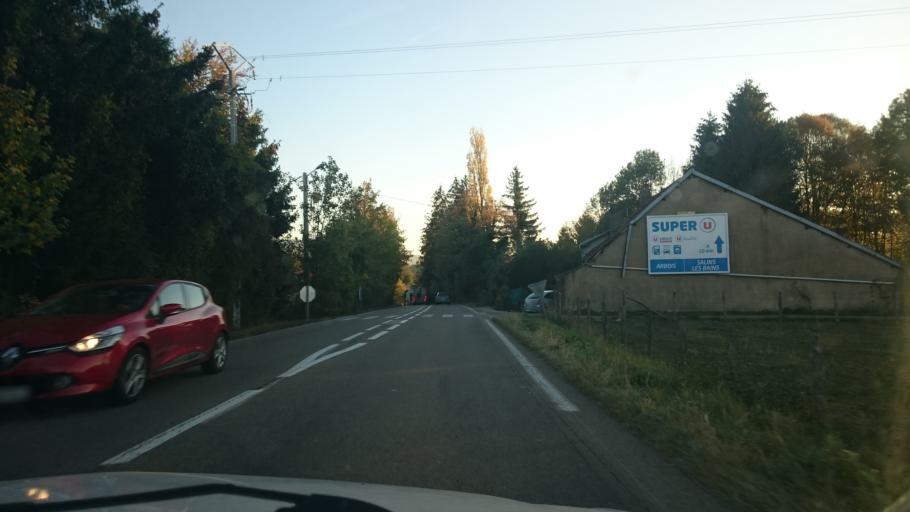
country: FR
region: Franche-Comte
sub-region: Departement du Doubs
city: Quingey
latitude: 47.0708
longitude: 5.8817
